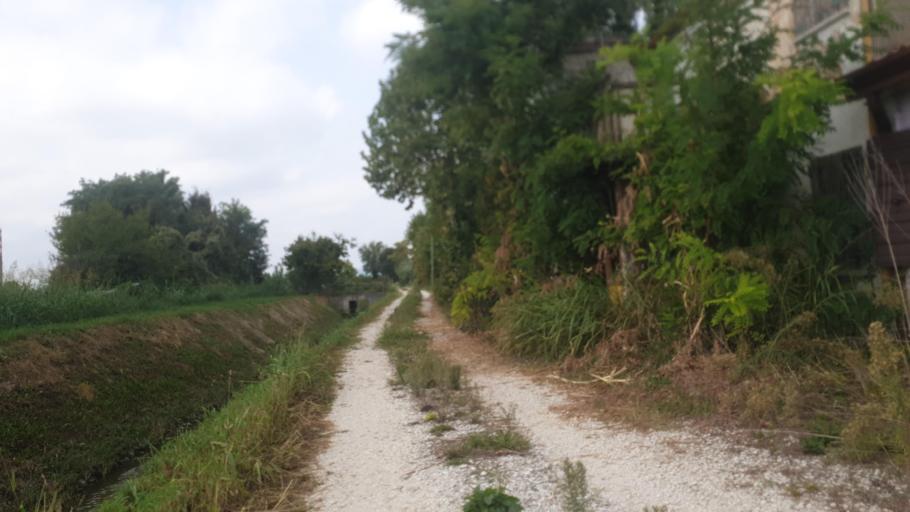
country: IT
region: Veneto
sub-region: Provincia di Padova
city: Albignasego
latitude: 45.3449
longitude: 11.8891
